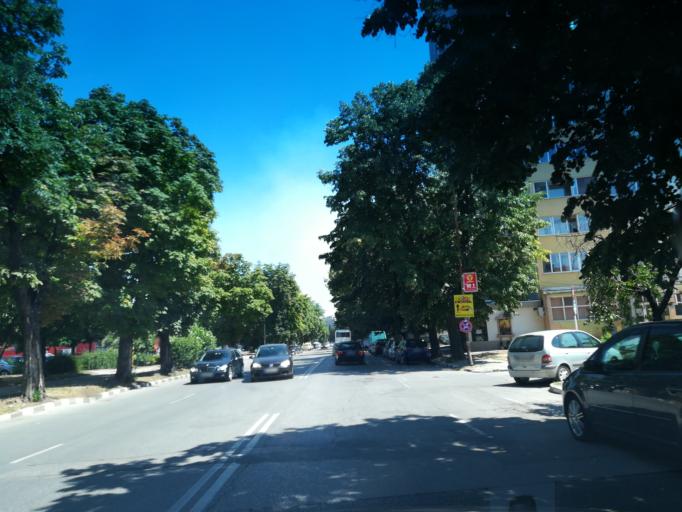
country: BG
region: Plovdiv
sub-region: Obshtina Asenovgrad
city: Asenovgrad
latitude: 42.0131
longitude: 24.8704
